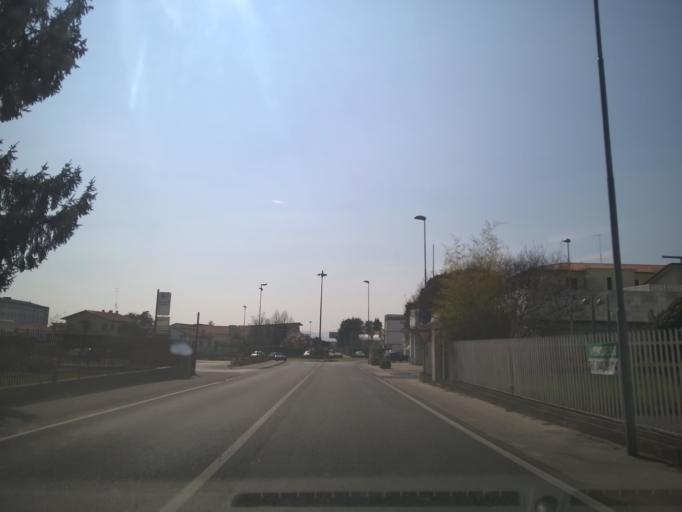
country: IT
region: Veneto
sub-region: Provincia di Vicenza
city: Thiene
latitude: 45.7138
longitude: 11.4693
